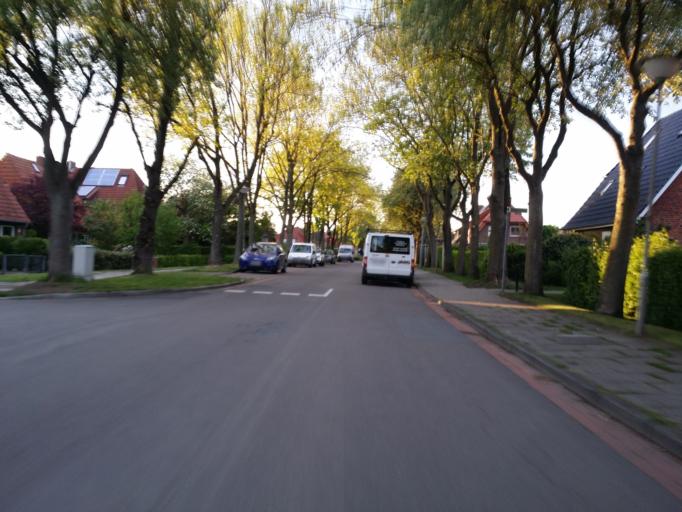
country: DE
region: Lower Saxony
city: Stuhr
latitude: 53.0546
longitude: 8.7656
